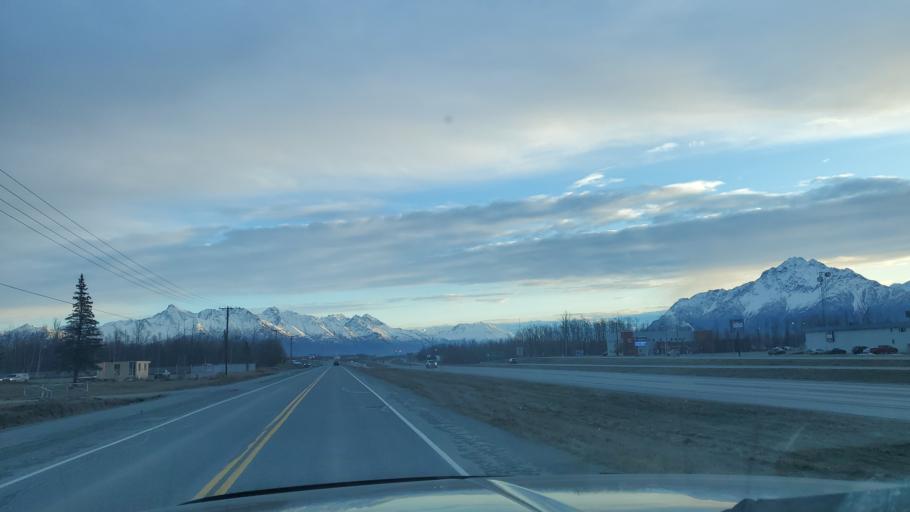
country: US
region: Alaska
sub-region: Matanuska-Susitna Borough
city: Lakes
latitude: 61.5632
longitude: -149.2904
